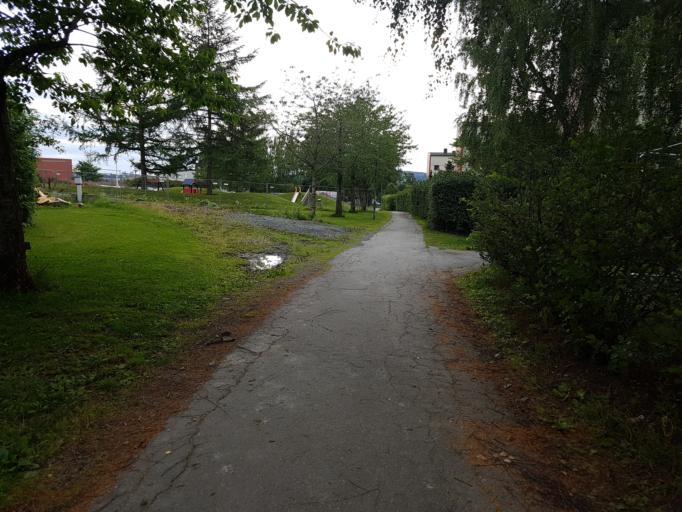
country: NO
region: Sor-Trondelag
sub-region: Trondheim
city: Trondheim
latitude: 63.4044
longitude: 10.4173
